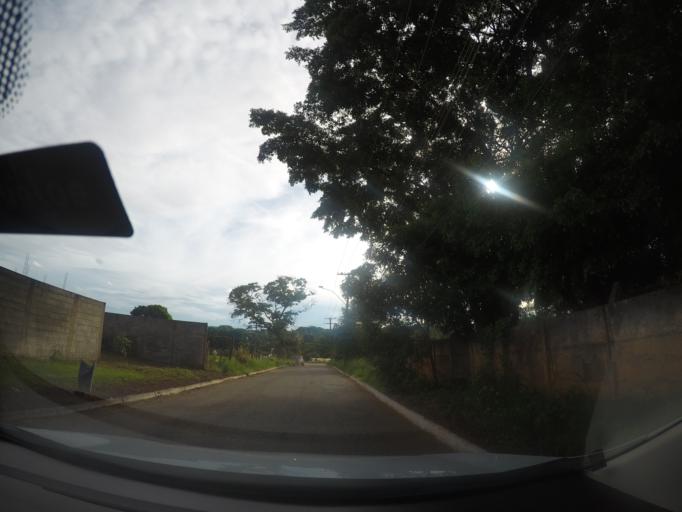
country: BR
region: Goias
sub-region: Goiania
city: Goiania
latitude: -16.6418
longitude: -49.3486
